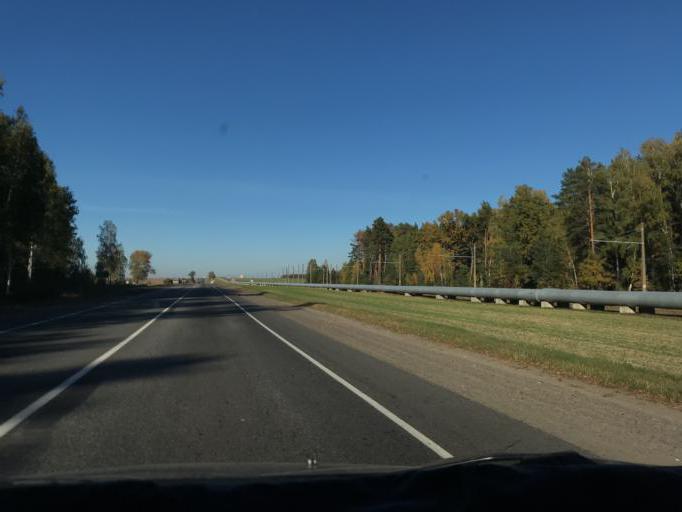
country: BY
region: Gomel
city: Mazyr
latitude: 51.9510
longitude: 29.2623
